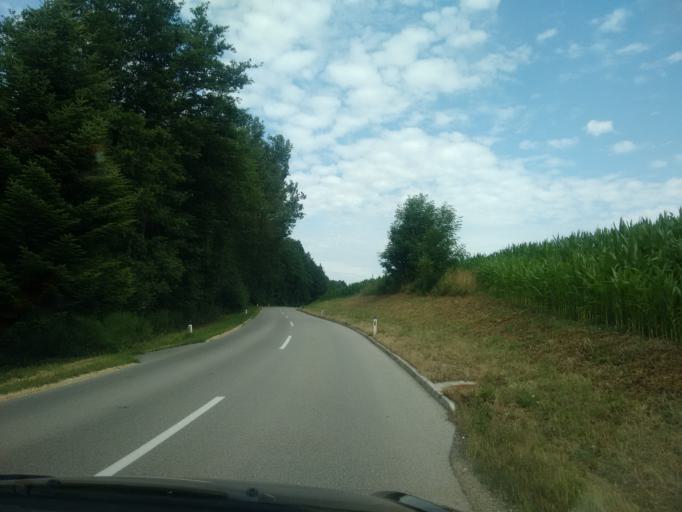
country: AT
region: Upper Austria
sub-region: Politischer Bezirk Grieskirchen
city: Grieskirchen
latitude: 48.1985
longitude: 13.8398
